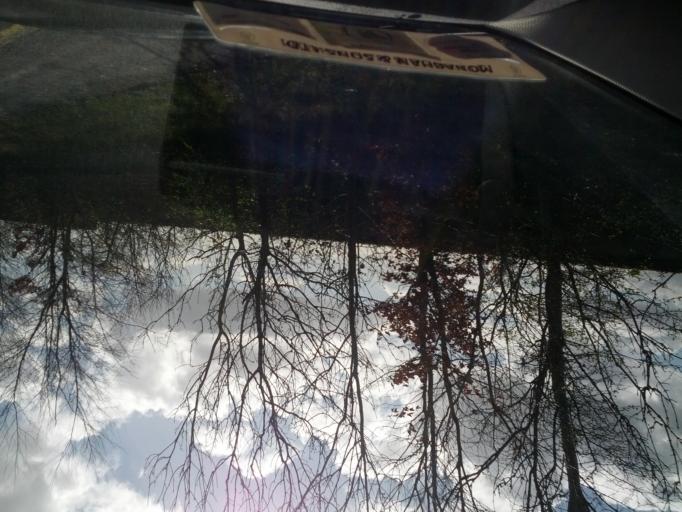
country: IE
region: Connaught
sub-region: County Galway
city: Claregalway
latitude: 53.2998
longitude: -8.9623
